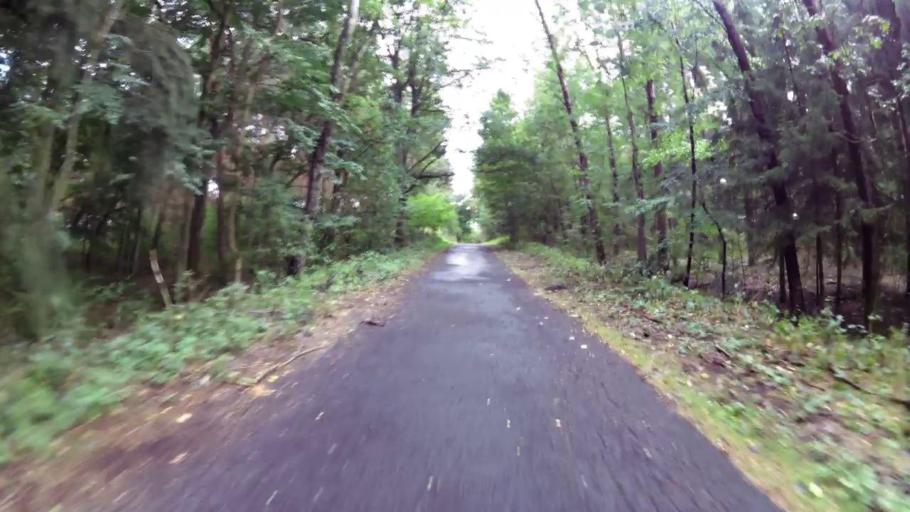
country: PL
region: West Pomeranian Voivodeship
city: Trzcinsko Zdroj
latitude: 52.8911
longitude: 14.7063
